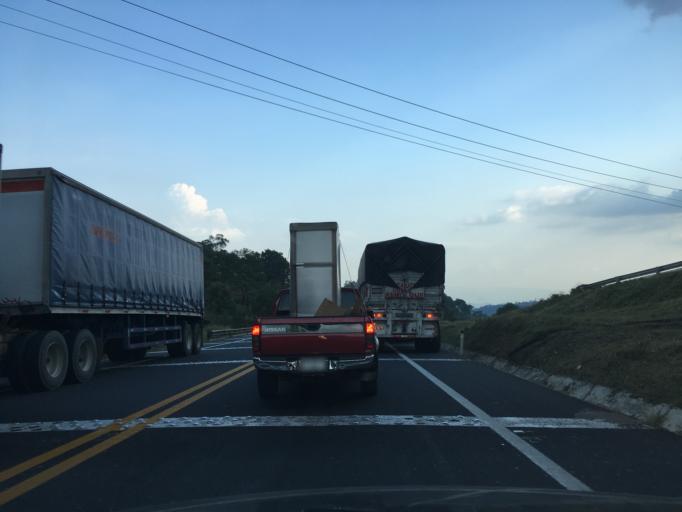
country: MX
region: Michoacan
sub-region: Uruapan
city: Toreo Bajo (El Toreo Bajo)
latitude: 19.4181
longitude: -101.9838
